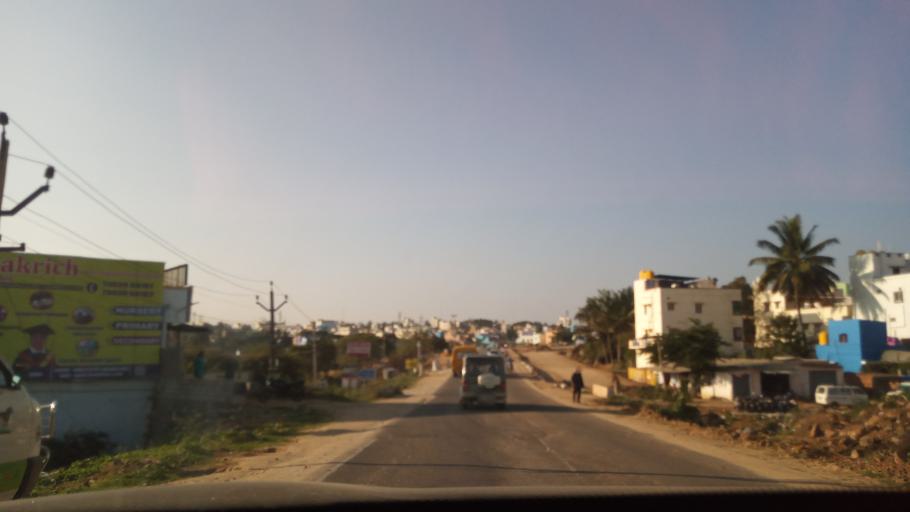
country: IN
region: Tamil Nadu
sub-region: Krishnagiri
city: Hosur
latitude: 12.7193
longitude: 77.8319
